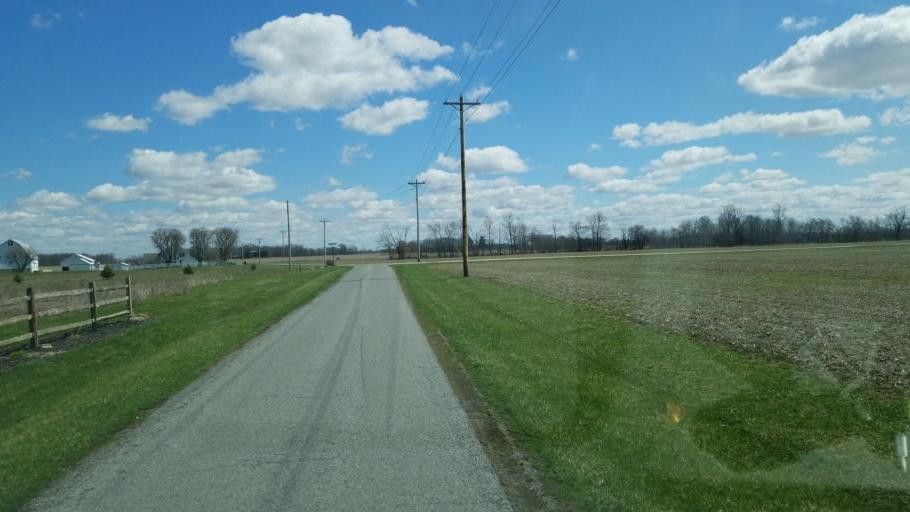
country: US
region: Ohio
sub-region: Hancock County
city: Arlington
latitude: 40.9527
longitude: -83.5239
